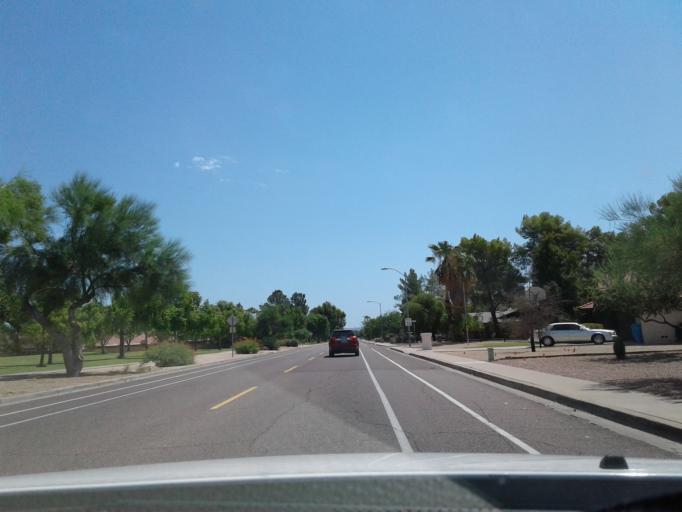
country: US
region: Arizona
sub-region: Maricopa County
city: Paradise Valley
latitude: 33.5899
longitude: -111.9901
